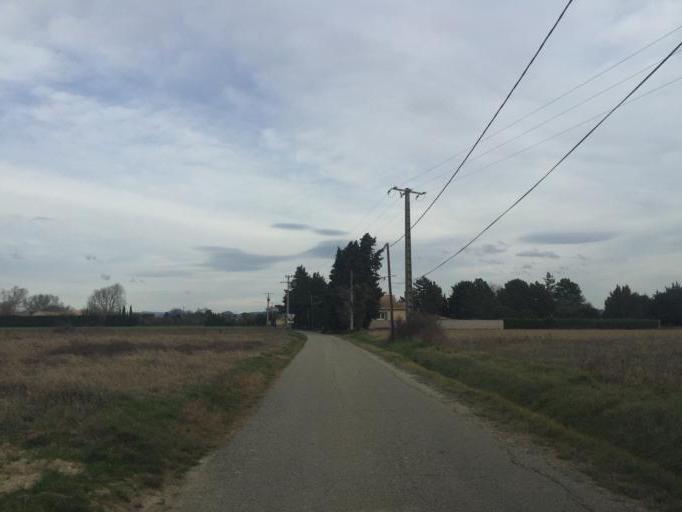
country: FR
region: Provence-Alpes-Cote d'Azur
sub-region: Departement du Vaucluse
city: Camaret-sur-Aigues
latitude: 44.1594
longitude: 4.8773
